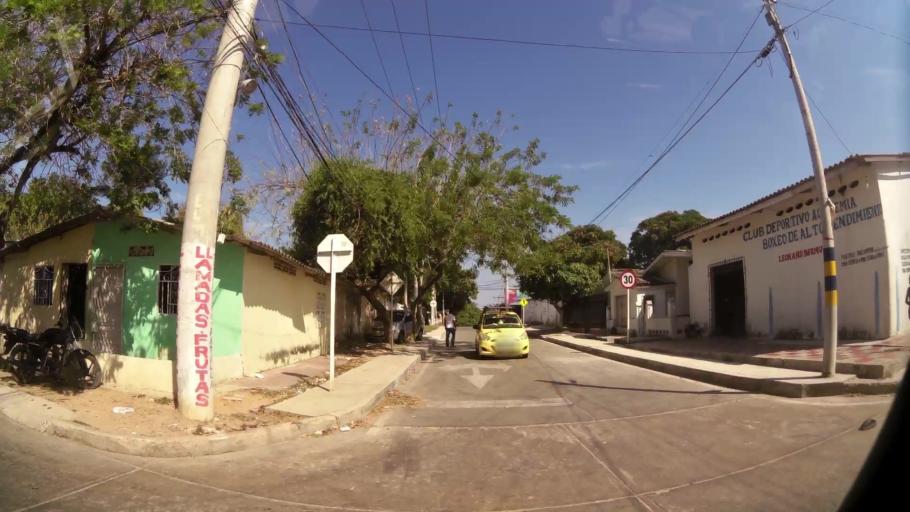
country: CO
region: Atlantico
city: Barranquilla
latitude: 10.9437
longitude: -74.8246
